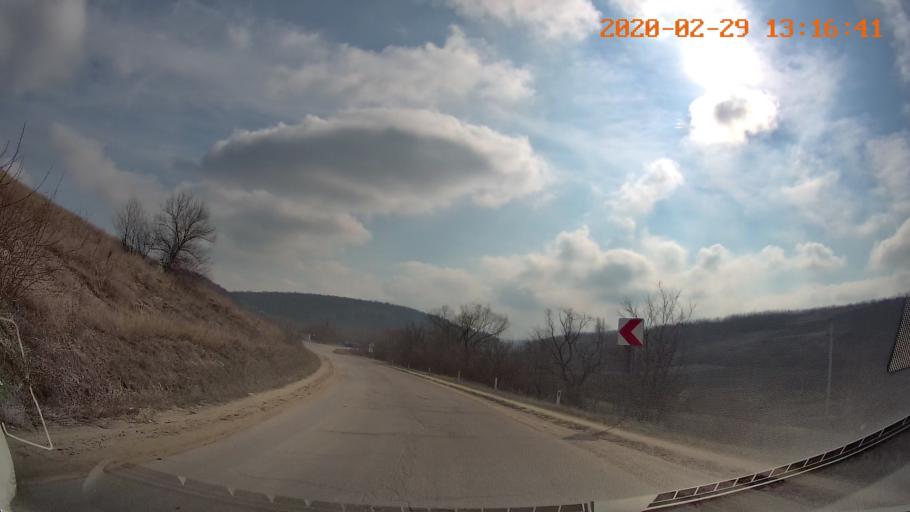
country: MD
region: Telenesti
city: Camenca
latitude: 48.0007
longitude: 28.6627
